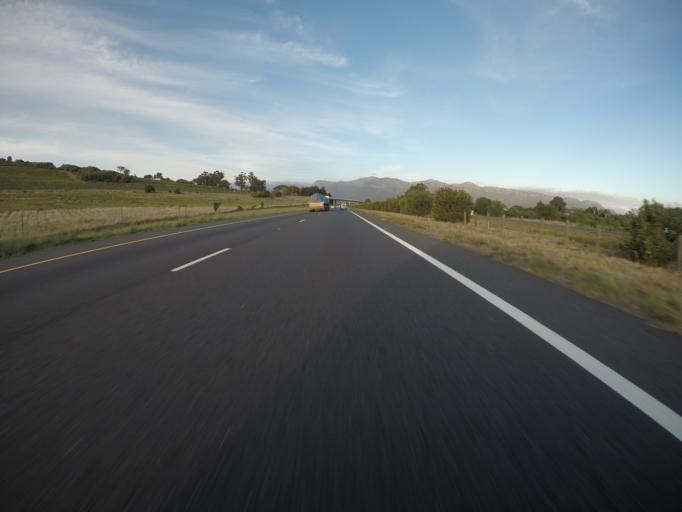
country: ZA
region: Western Cape
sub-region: Cape Winelands District Municipality
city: Paarl
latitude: -33.7851
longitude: 18.9383
